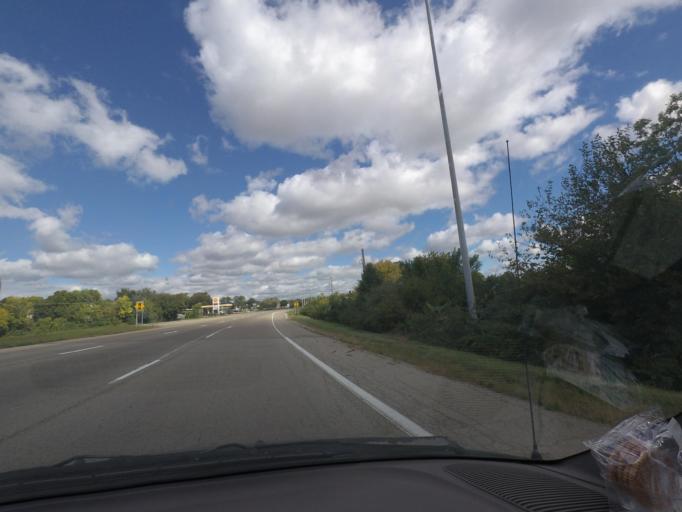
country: US
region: Ohio
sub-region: Clark County
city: Park Layne
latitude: 39.8688
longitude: -84.0555
